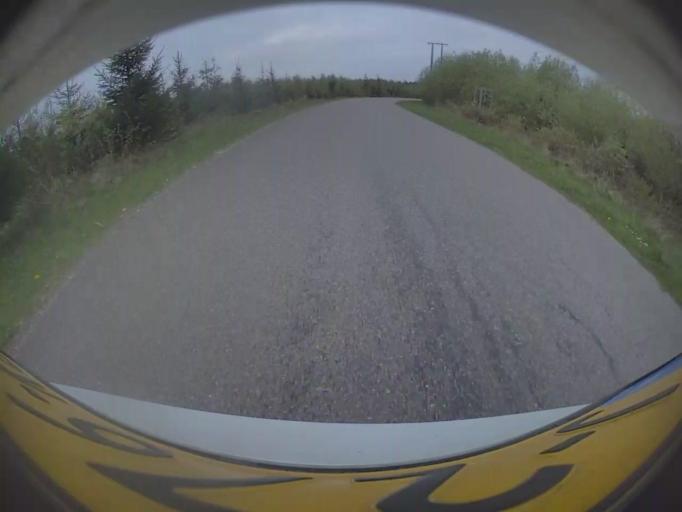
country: BE
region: Wallonia
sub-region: Province du Luxembourg
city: La Roche-en-Ardenne
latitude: 50.2263
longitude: 5.6076
